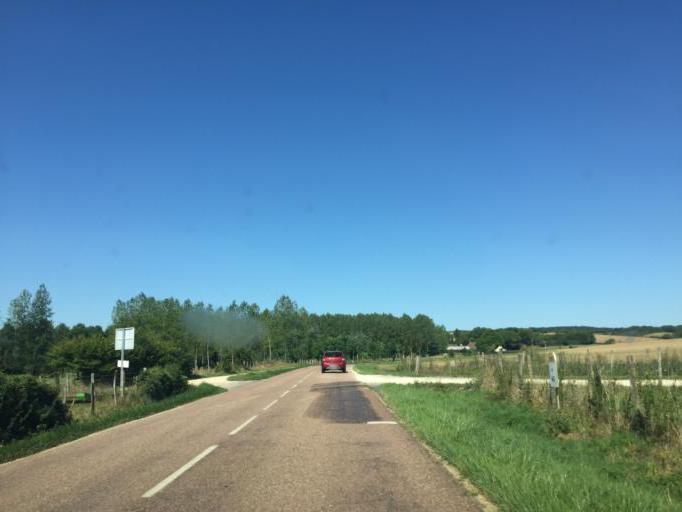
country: FR
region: Bourgogne
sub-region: Departement de l'Yonne
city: Fontenailles
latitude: 47.4776
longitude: 3.4315
